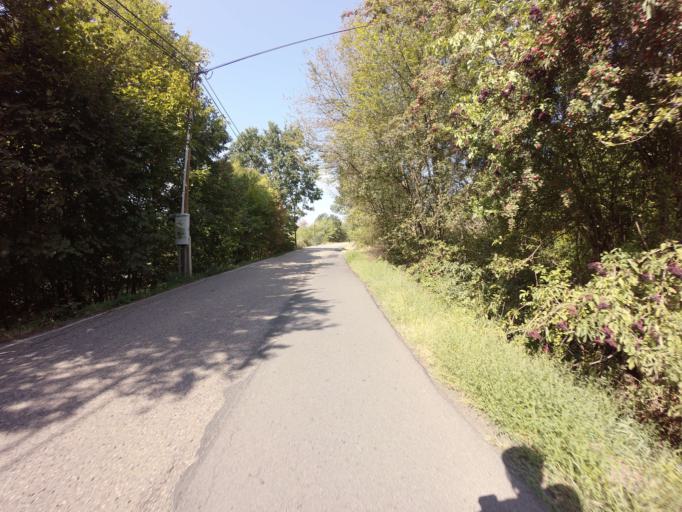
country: CZ
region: Central Bohemia
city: Kamenny Privoz
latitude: 49.8613
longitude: 14.5388
